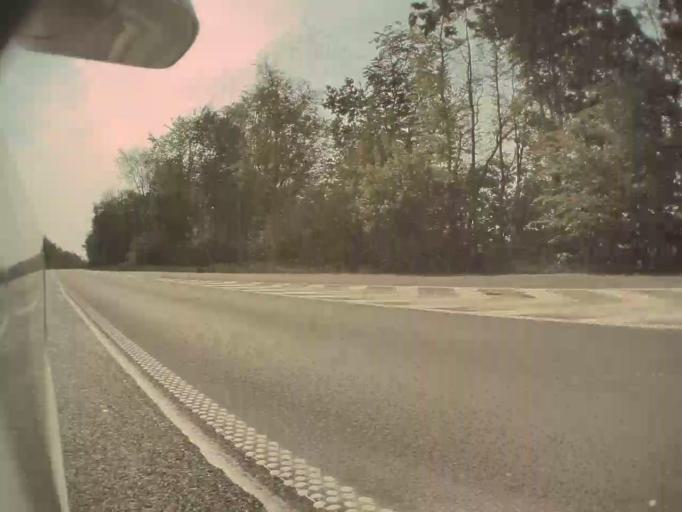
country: BE
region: Wallonia
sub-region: Province de Namur
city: Ciney
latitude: 50.2906
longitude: 5.1098
